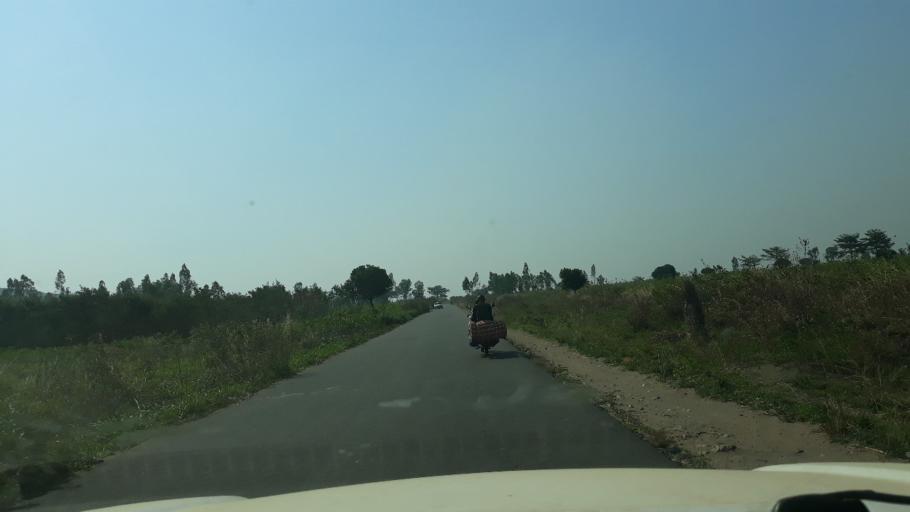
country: CD
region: South Kivu
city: Uvira
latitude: -3.2126
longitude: 29.1645
